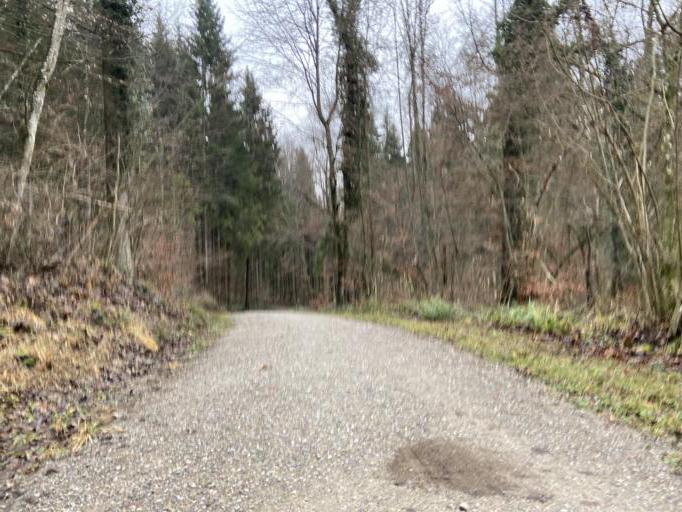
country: CH
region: Zurich
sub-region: Bezirk Winterthur
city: Toess (Kreis 4) / Vorder-Daettnau
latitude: 47.4883
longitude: 8.6845
